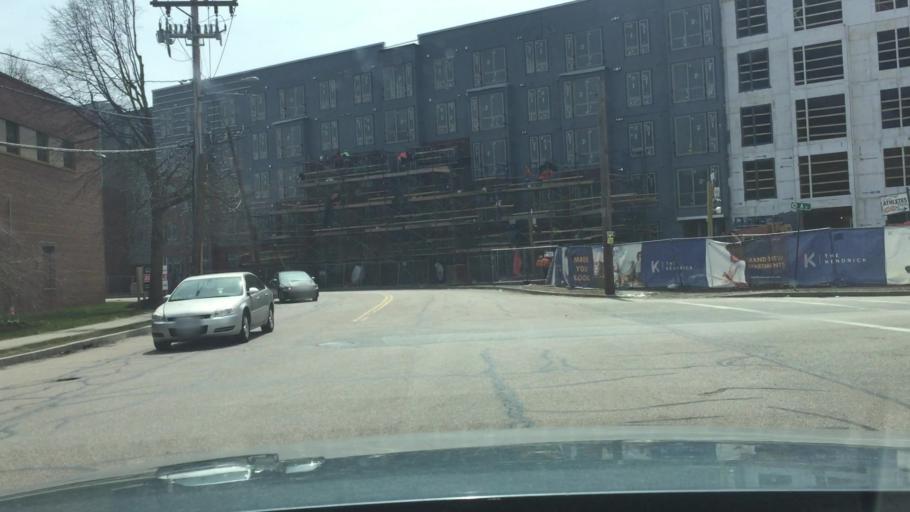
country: US
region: Massachusetts
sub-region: Norfolk County
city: Needham
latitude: 42.3025
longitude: -71.2157
